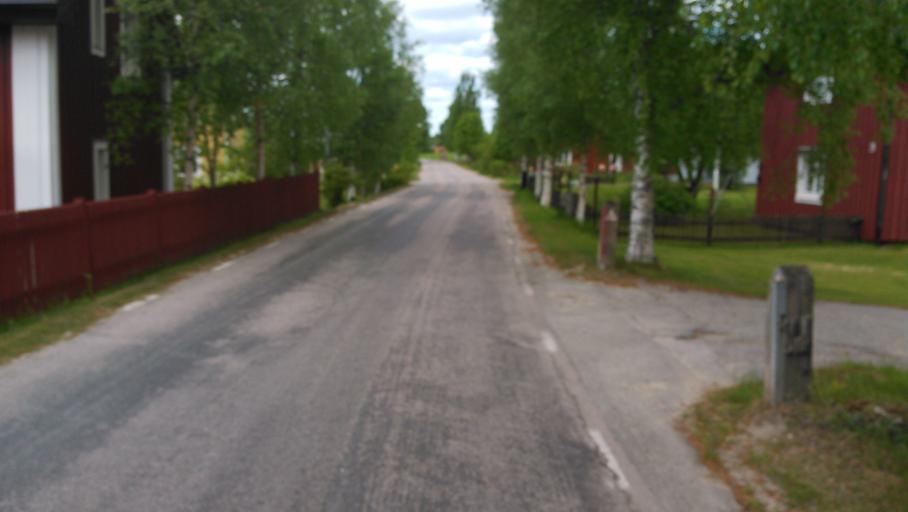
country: SE
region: Vaesterbotten
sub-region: Umea Kommun
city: Roback
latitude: 63.8657
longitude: 20.0776
